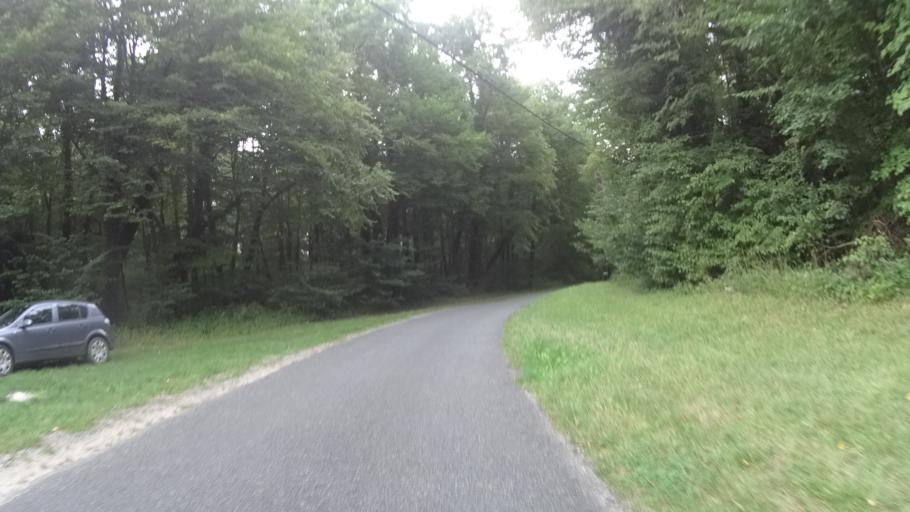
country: FR
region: Picardie
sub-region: Departement de l'Oise
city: Ver-sur-Launette
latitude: 49.1641
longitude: 2.6791
